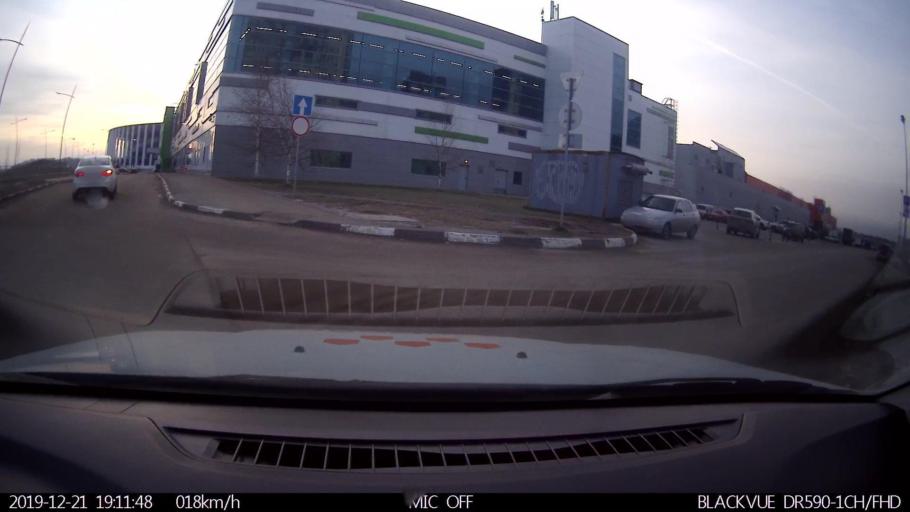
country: RU
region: Nizjnij Novgorod
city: Nizhniy Novgorod
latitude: 56.3412
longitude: 43.9564
